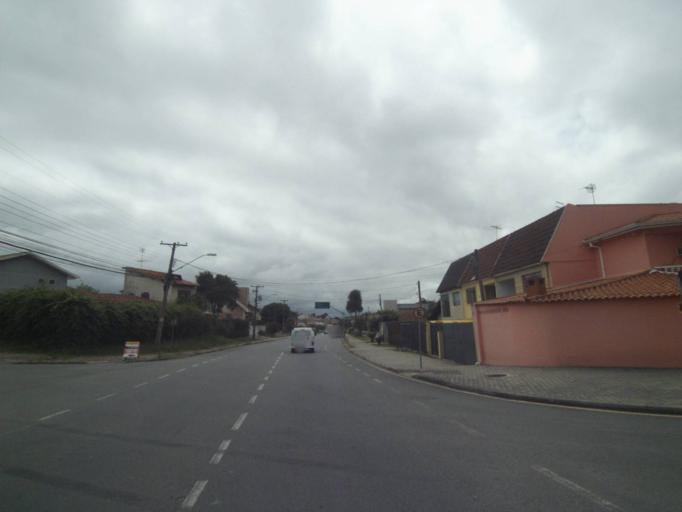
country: BR
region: Parana
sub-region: Pinhais
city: Pinhais
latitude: -25.4370
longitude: -49.2304
